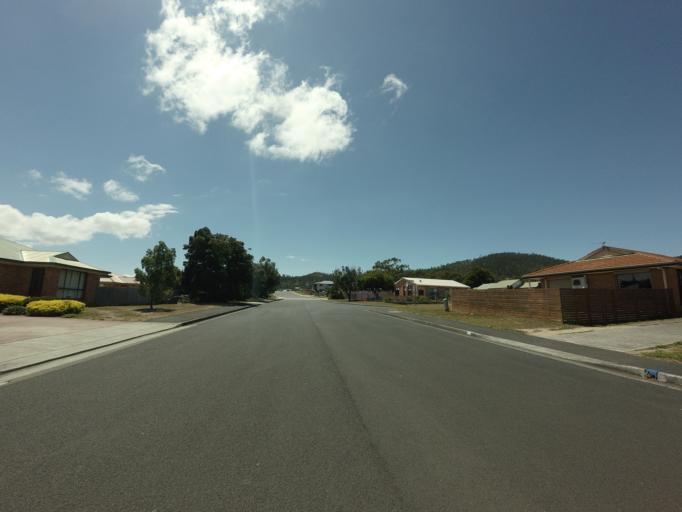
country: AU
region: Tasmania
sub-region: Clarence
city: Rokeby
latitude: -42.9014
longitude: 147.4515
